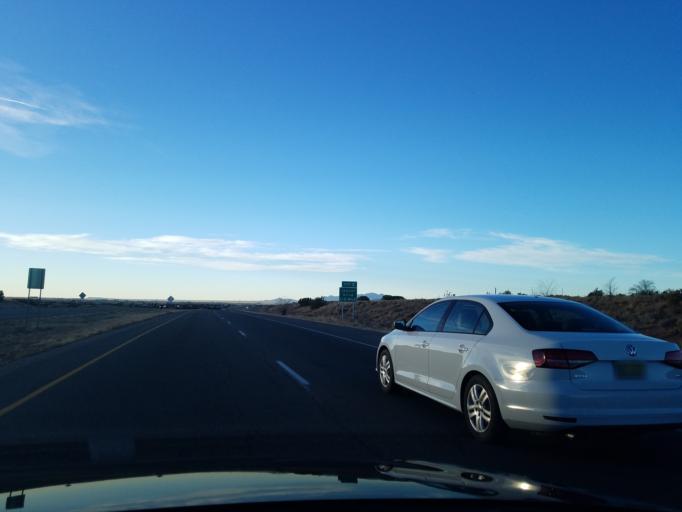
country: US
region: New Mexico
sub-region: Santa Fe County
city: Agua Fria
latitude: 35.6288
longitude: -106.0710
